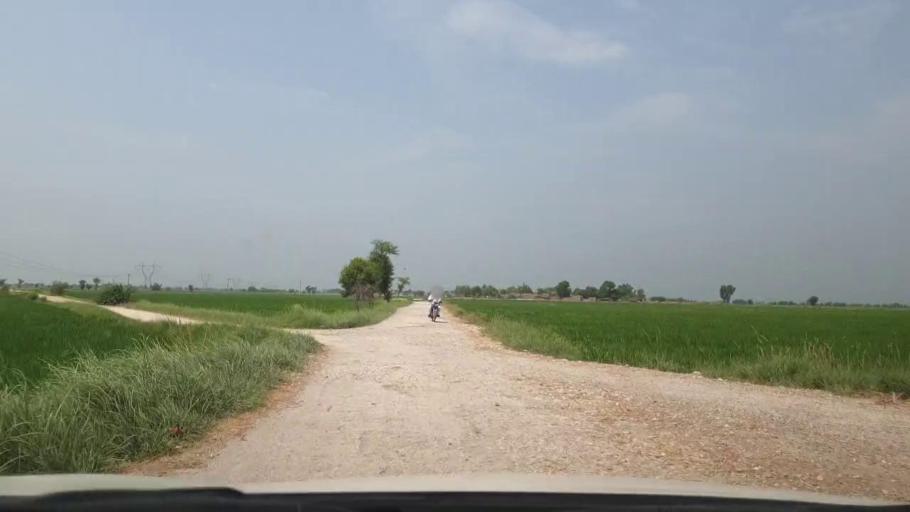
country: PK
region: Sindh
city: Dokri
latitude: 27.3925
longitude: 68.0537
